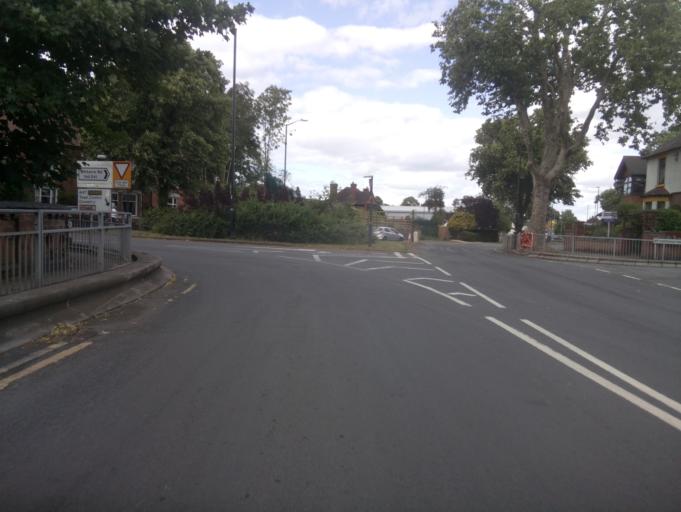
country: GB
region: England
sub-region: Warwickshire
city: Nuneaton
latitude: 52.5272
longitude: -1.4583
